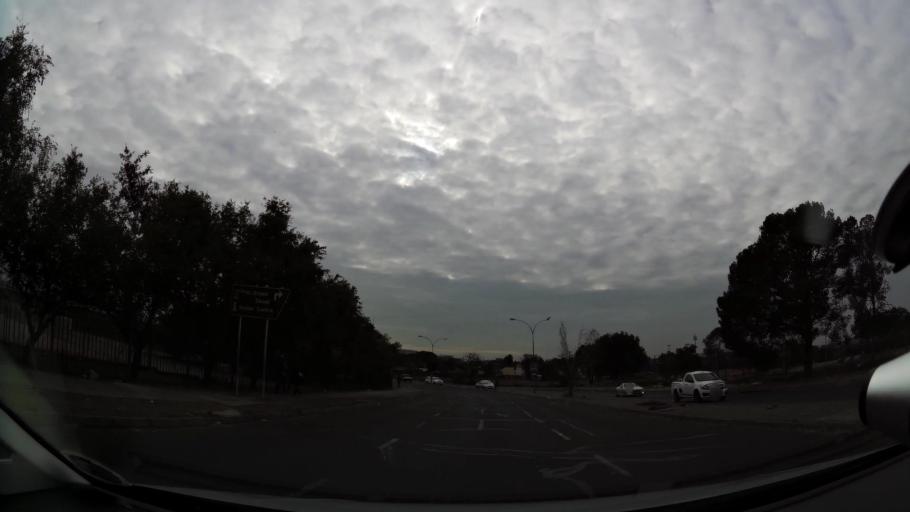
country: ZA
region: Orange Free State
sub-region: Mangaung Metropolitan Municipality
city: Bloemfontein
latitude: -29.1257
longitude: 26.2105
